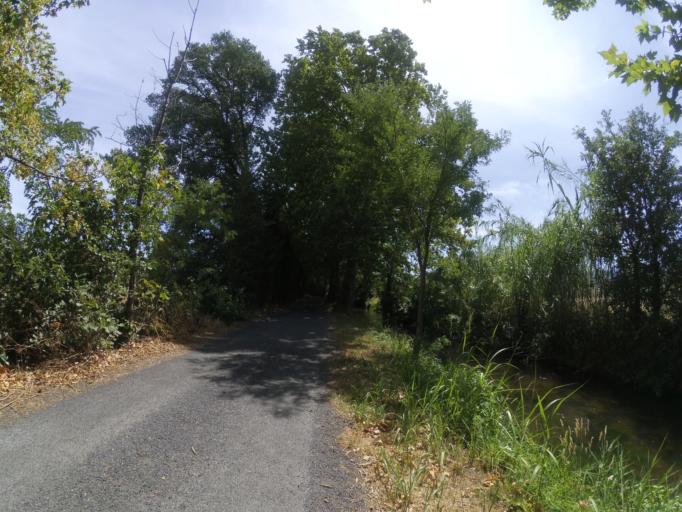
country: FR
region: Languedoc-Roussillon
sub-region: Departement des Pyrenees-Orientales
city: Ille-sur-Tet
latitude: 42.6803
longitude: 2.6447
